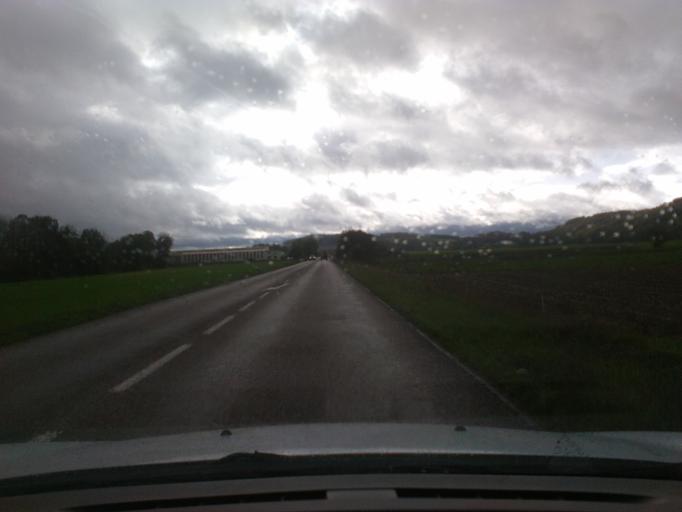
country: FR
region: Lorraine
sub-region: Departement des Vosges
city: Charmes
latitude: 48.3904
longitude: 6.2593
